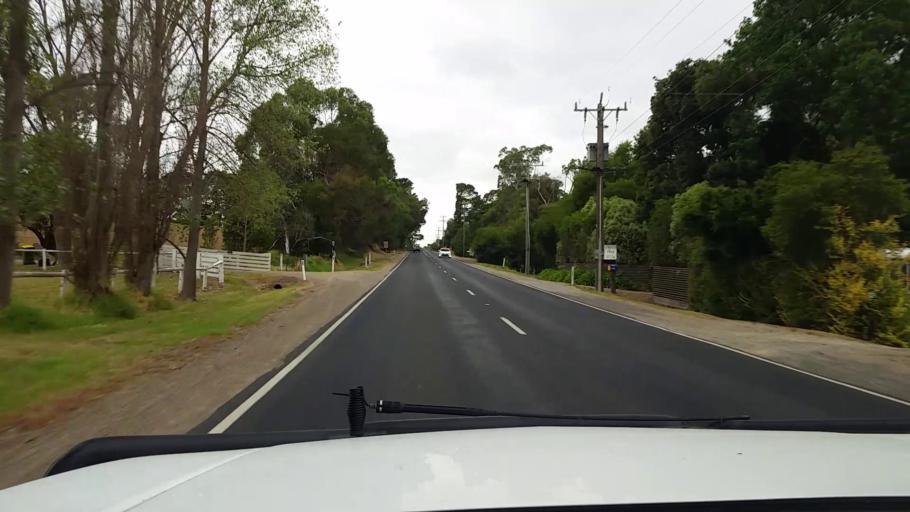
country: AU
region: Victoria
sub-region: Mornington Peninsula
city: Langwarrin South
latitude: -38.1996
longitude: 145.1978
